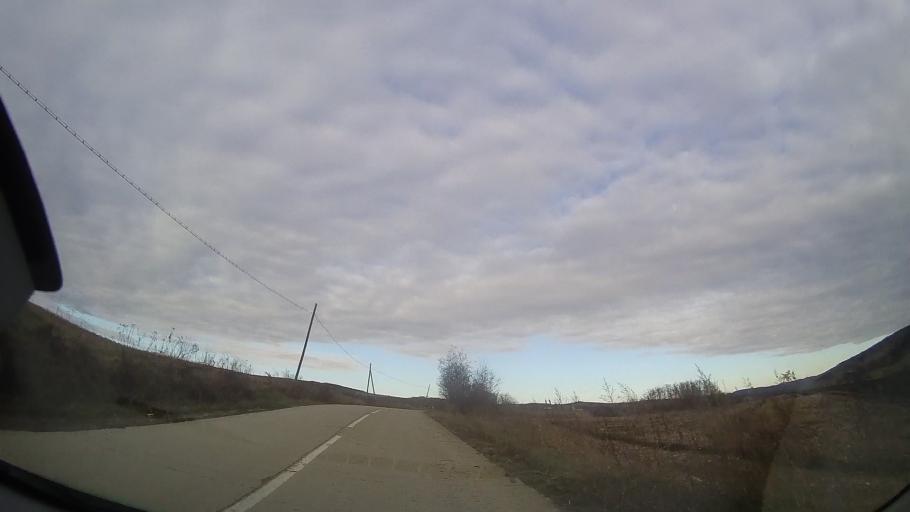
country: RO
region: Bistrita-Nasaud
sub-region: Comuna Sanmihaiu de Campie
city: Sanmihaiu de Campie
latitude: 46.8847
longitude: 24.3327
